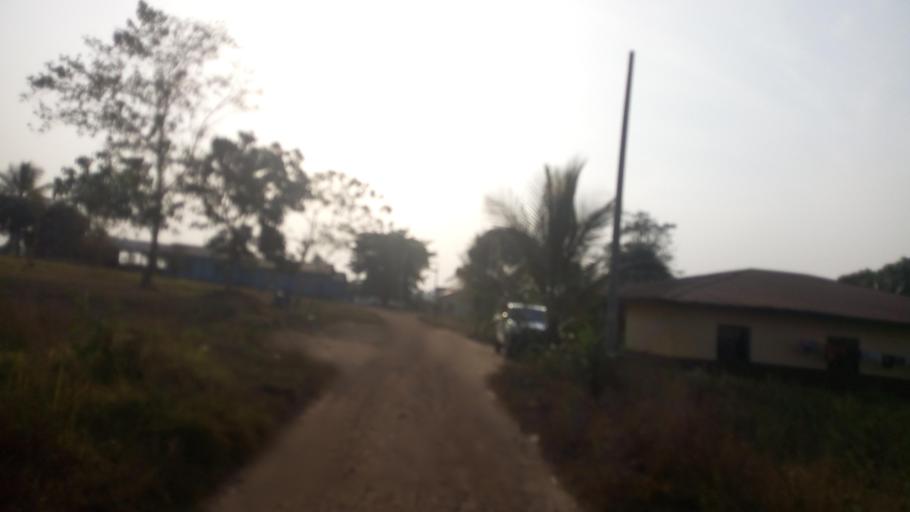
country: SL
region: Southern Province
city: Mogbwemo
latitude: 7.6016
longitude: -12.1770
